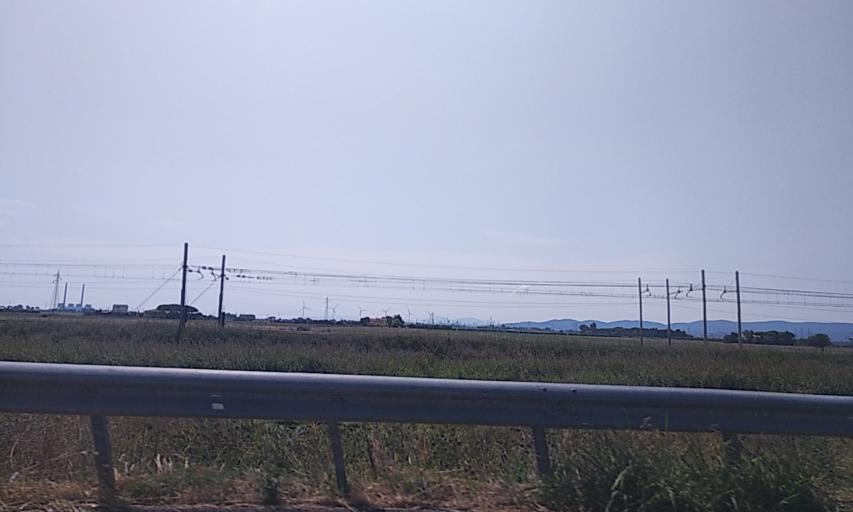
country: IT
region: Tuscany
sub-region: Provincia di Livorno
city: Venturina
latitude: 43.0016
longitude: 10.6134
